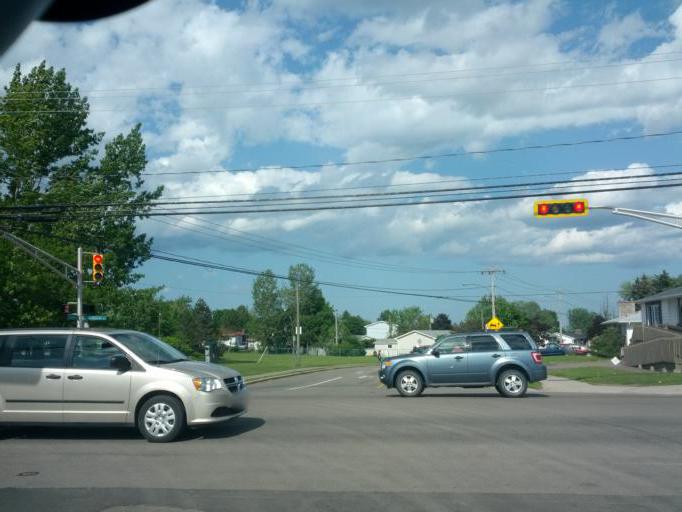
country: CA
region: New Brunswick
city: Moncton
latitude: 46.1096
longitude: -64.8238
